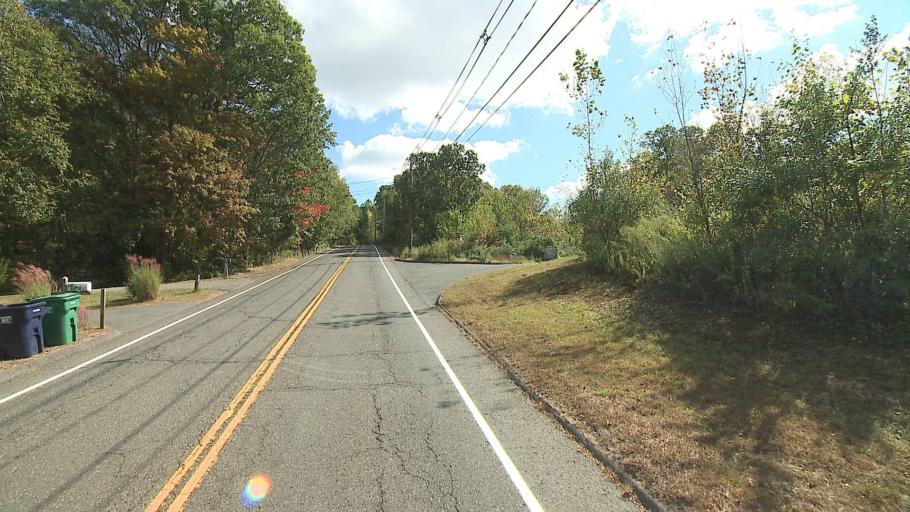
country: US
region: Connecticut
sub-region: New Haven County
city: Oxford
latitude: 41.4316
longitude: -73.1074
